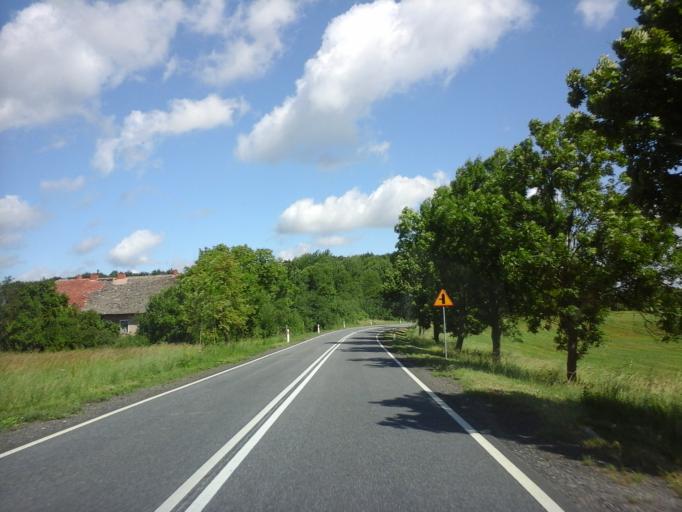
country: PL
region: West Pomeranian Voivodeship
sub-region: Powiat stargardzki
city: Insko
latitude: 53.4706
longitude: 15.5782
